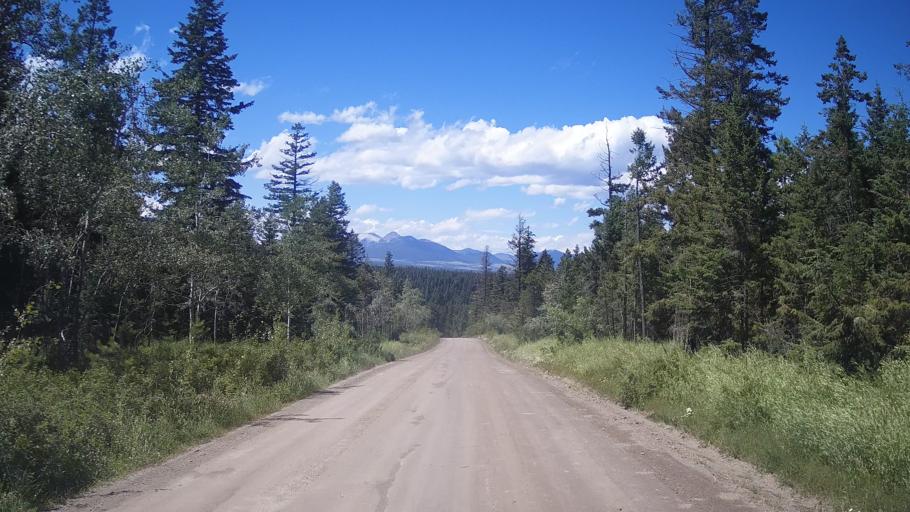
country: CA
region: British Columbia
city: Cache Creek
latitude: 51.1538
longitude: -121.5425
